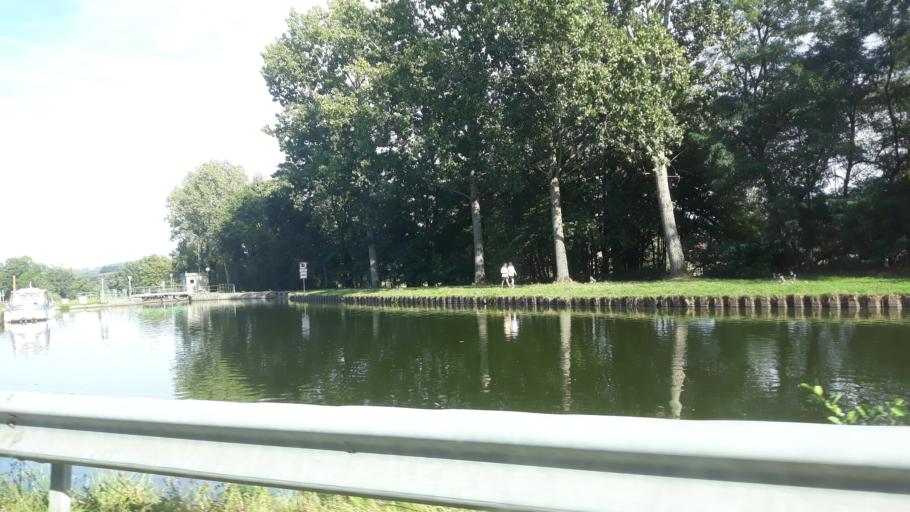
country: FR
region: Bourgogne
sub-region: Departement de Saone-et-Loire
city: Ecuisses
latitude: 46.7672
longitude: 4.5269
